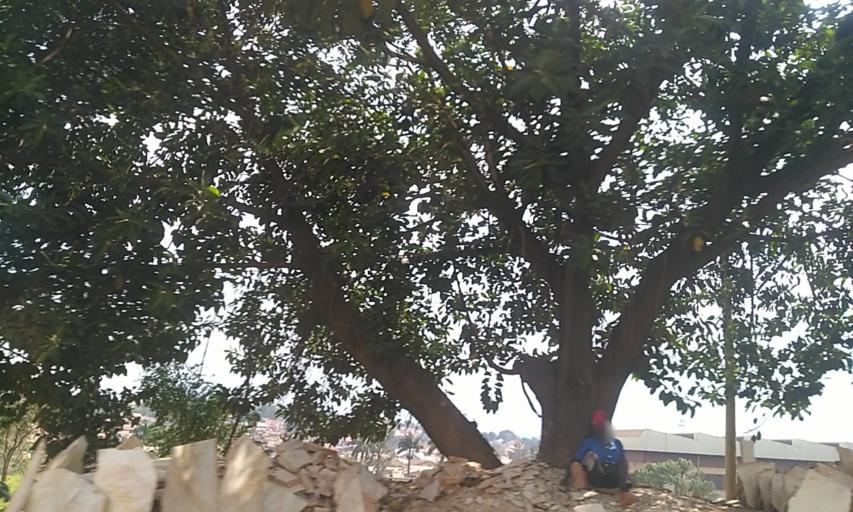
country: UG
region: Central Region
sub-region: Kampala District
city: Kampala
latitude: 0.2942
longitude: 32.5564
